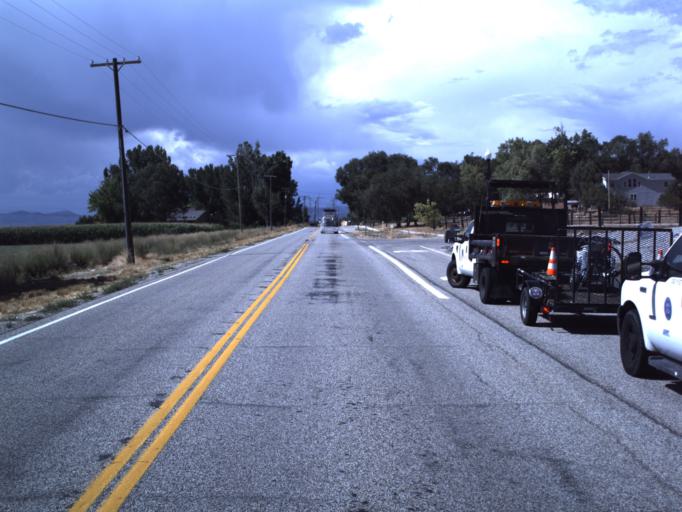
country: US
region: Utah
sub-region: Box Elder County
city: Honeyville
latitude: 41.6165
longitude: -112.0672
